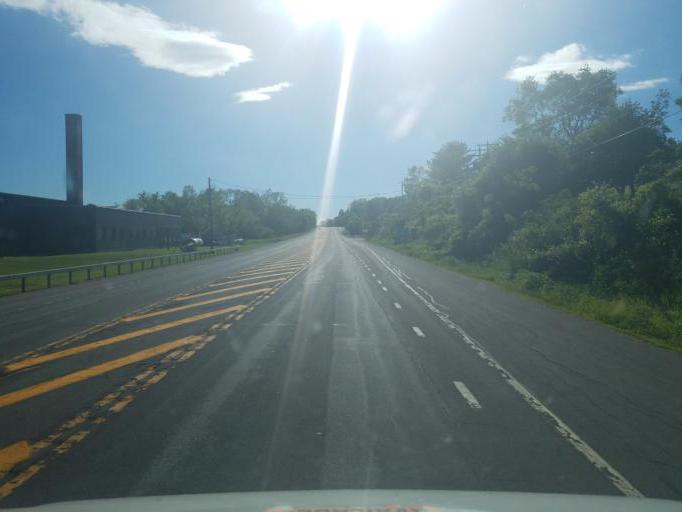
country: US
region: New York
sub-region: Herkimer County
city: Little Falls
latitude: 43.0231
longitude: -74.9085
